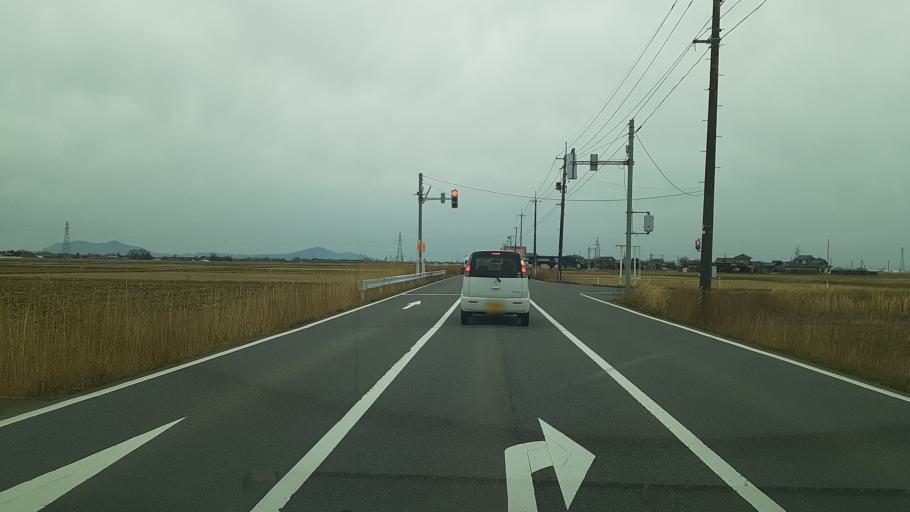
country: JP
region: Niigata
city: Niitsu-honcho
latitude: 37.8161
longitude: 139.0848
